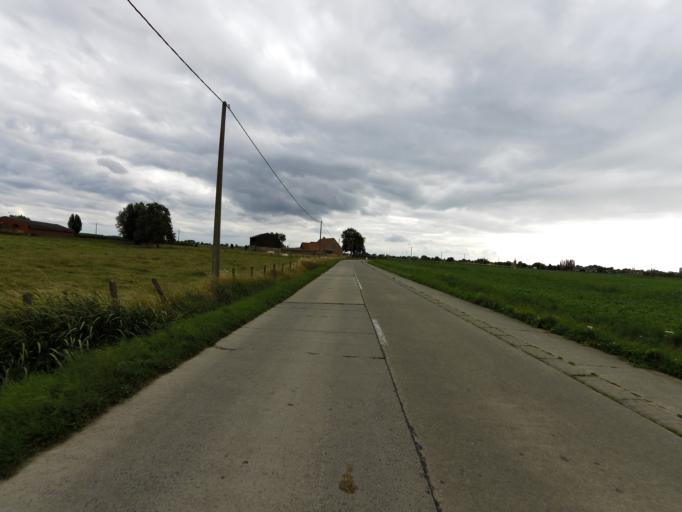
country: BE
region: Flanders
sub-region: Provincie West-Vlaanderen
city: Staden
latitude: 50.9843
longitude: 3.0310
